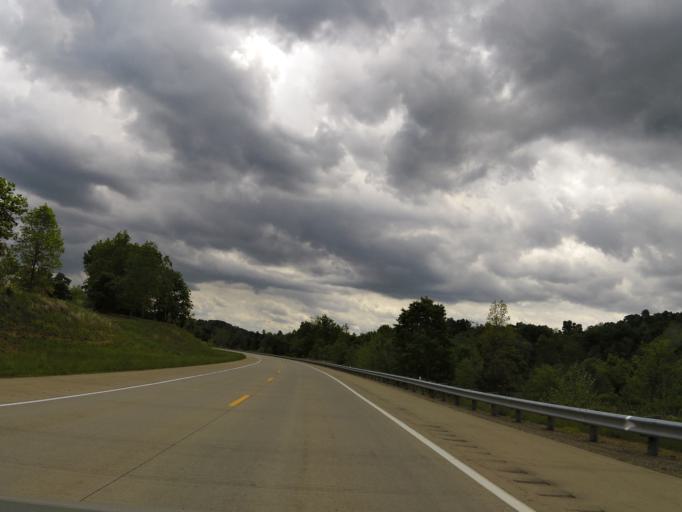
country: US
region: West Virginia
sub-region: Mason County
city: New Haven
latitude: 38.9805
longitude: -81.8680
